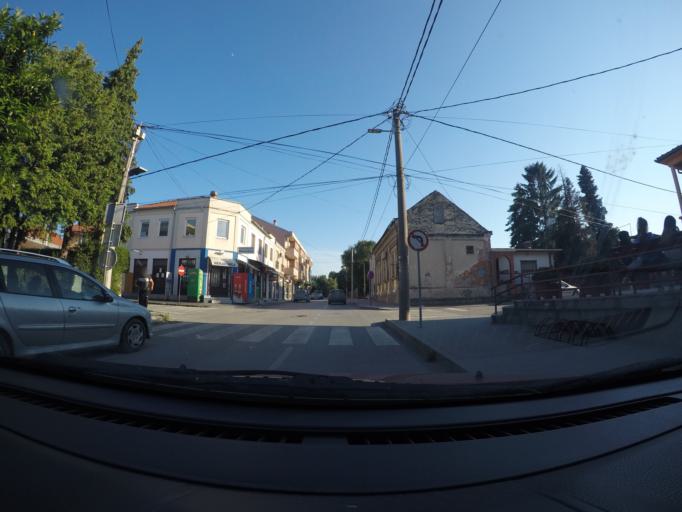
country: RS
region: Central Serbia
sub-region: Branicevski Okrug
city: Veliko Gradiste
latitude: 44.7636
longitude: 21.5155
